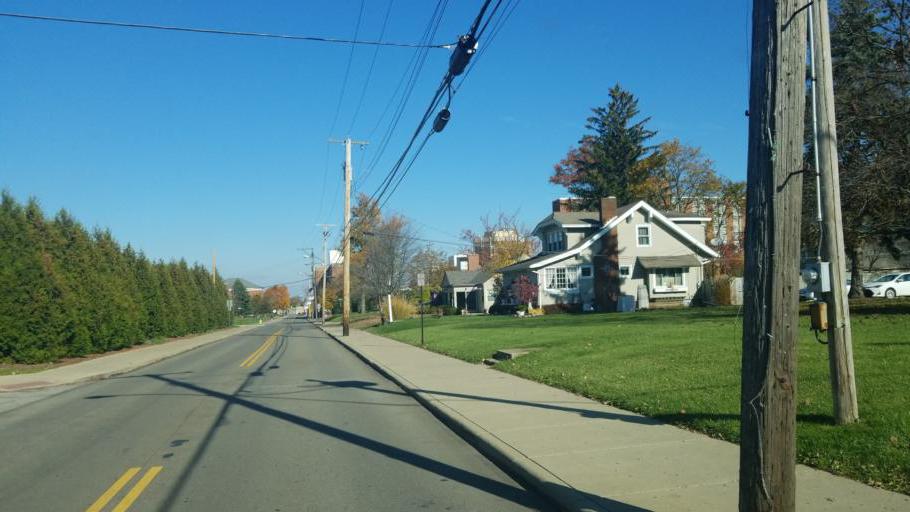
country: US
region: Ohio
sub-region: Ashland County
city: Ashland
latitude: 40.8585
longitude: -82.3223
